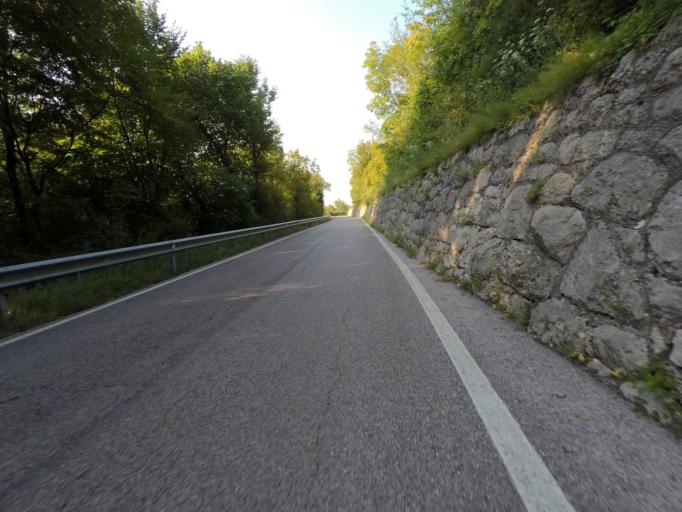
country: IT
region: Friuli Venezia Giulia
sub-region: Provincia di Udine
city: Forgaria nel Friuli
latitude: 46.2351
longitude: 13.0297
